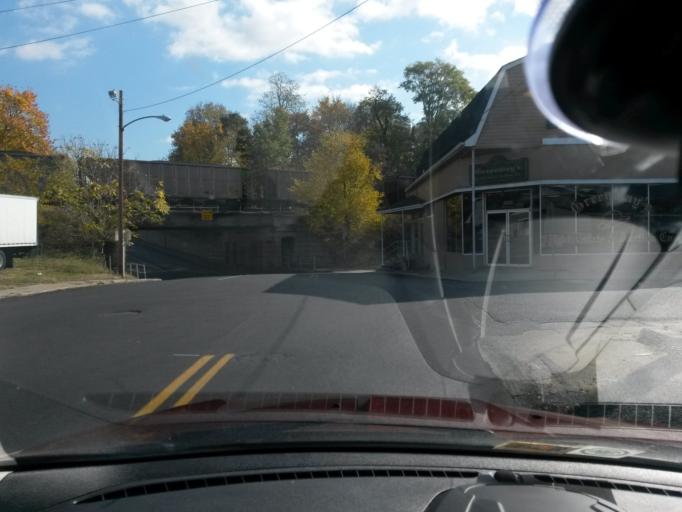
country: US
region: Virginia
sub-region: City of Covington
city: Covington
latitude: 37.7926
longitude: -79.9938
